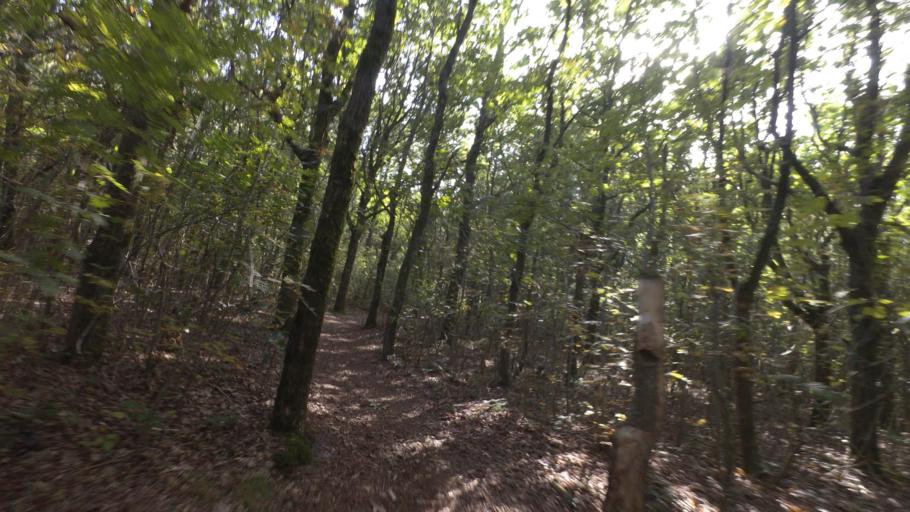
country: NL
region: Friesland
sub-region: Gemeente Ameland
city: Hollum
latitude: 53.4487
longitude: 5.7014
